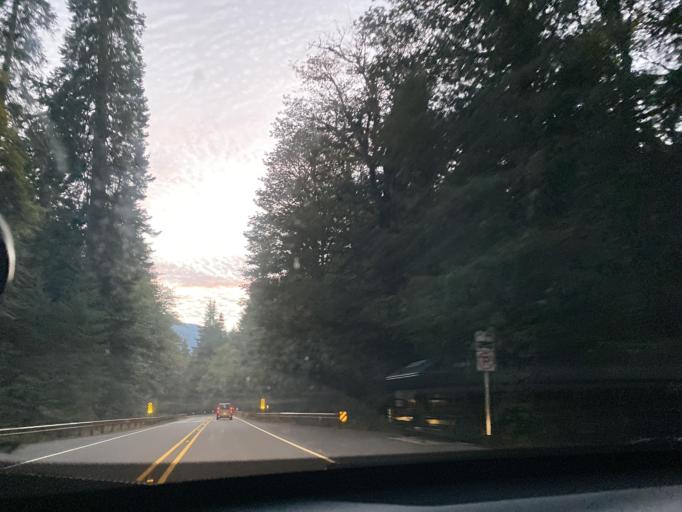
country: CA
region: British Columbia
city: Sooke
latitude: 48.0550
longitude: -123.7929
